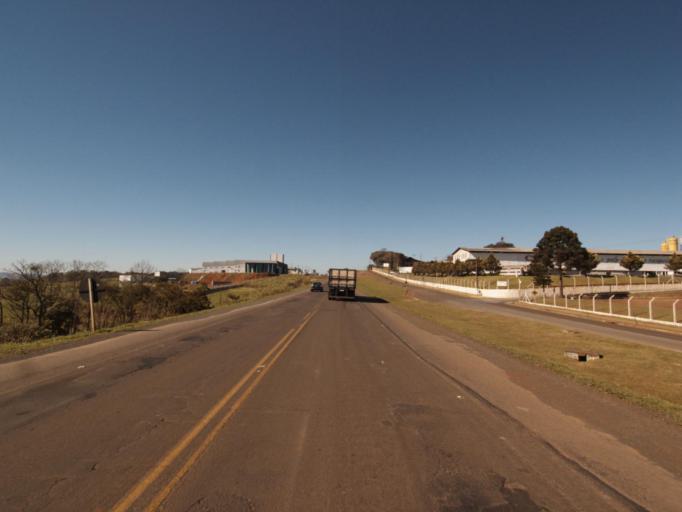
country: BR
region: Santa Catarina
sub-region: Chapeco
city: Chapeco
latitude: -26.8627
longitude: -52.9758
